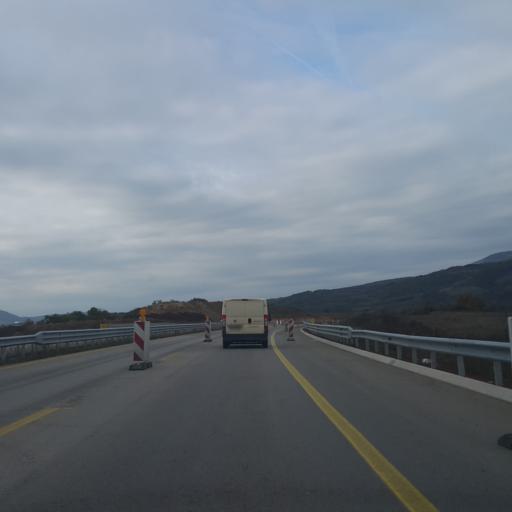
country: RS
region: Central Serbia
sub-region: Pirotski Okrug
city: Bela Palanka
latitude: 43.2254
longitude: 22.3878
